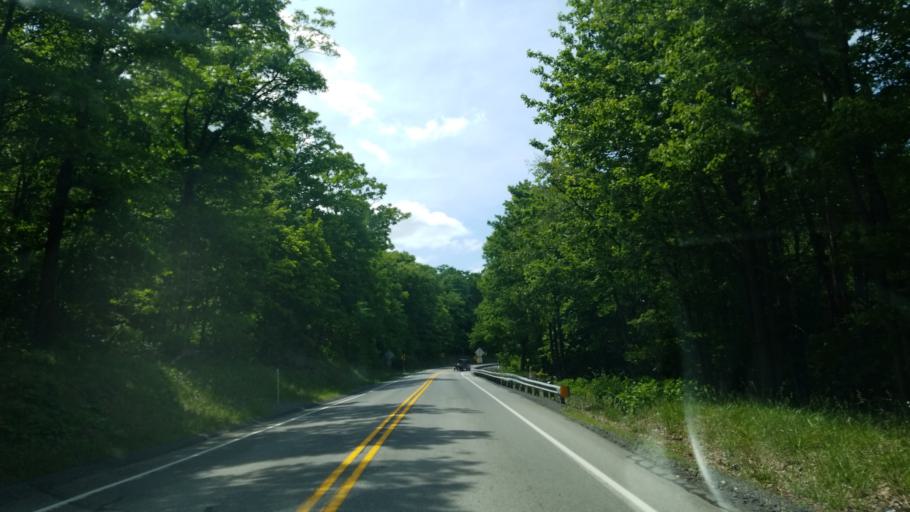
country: US
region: Pennsylvania
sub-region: Blair County
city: Tyrone
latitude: 40.7037
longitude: -78.2911
